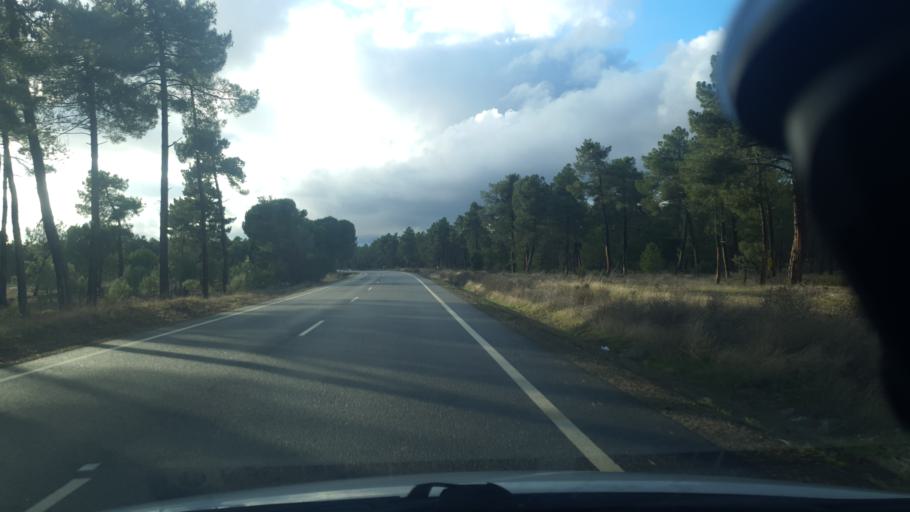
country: ES
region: Castille and Leon
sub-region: Provincia de Segovia
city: Nava de la Asuncion
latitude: 41.1558
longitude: -4.5202
